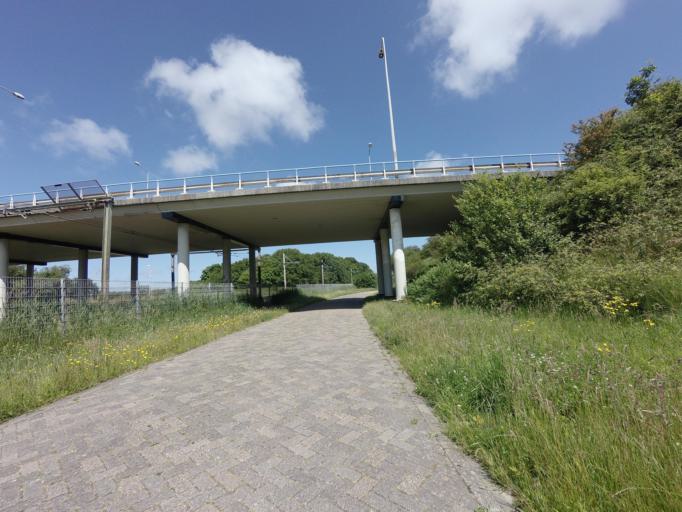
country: NL
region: North Holland
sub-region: Gemeente Den Helder
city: Den Helder
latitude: 52.9405
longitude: 4.7608
